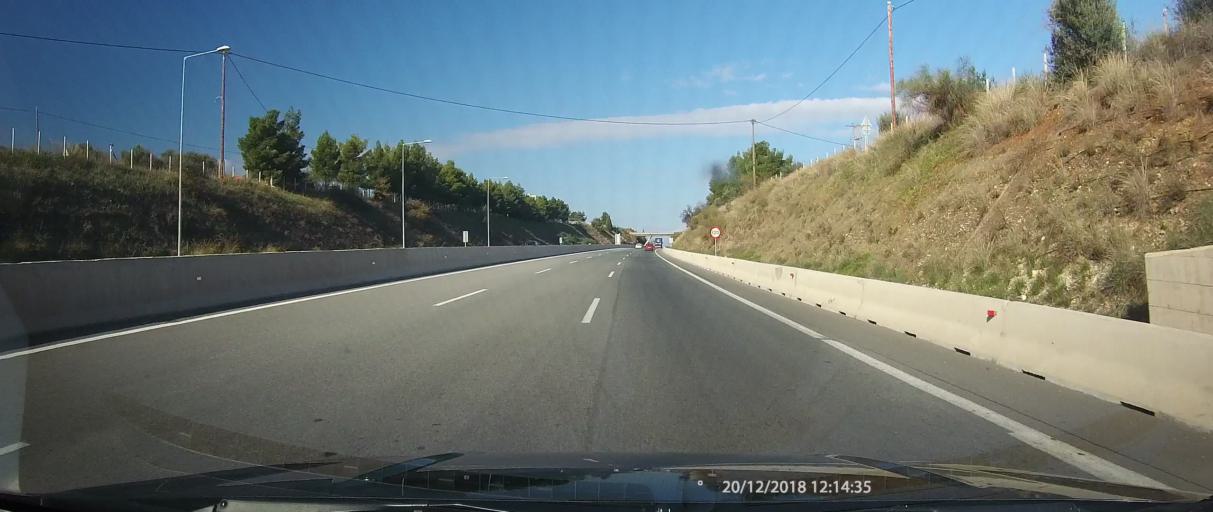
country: GR
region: West Greece
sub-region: Nomos Achaias
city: Aigio
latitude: 38.2384
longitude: 22.0768
